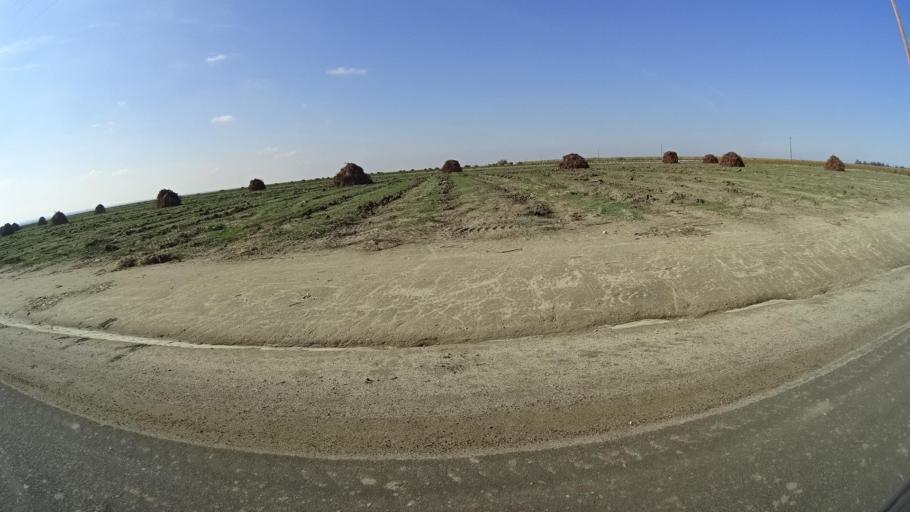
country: US
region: California
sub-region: Kern County
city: Arvin
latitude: 35.2808
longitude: -118.7708
